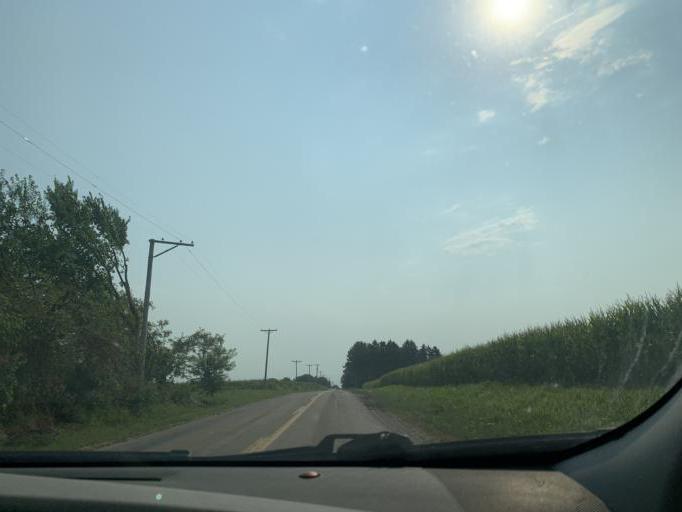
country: US
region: Illinois
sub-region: Whiteside County
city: Morrison
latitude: 41.8479
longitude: -89.8473
